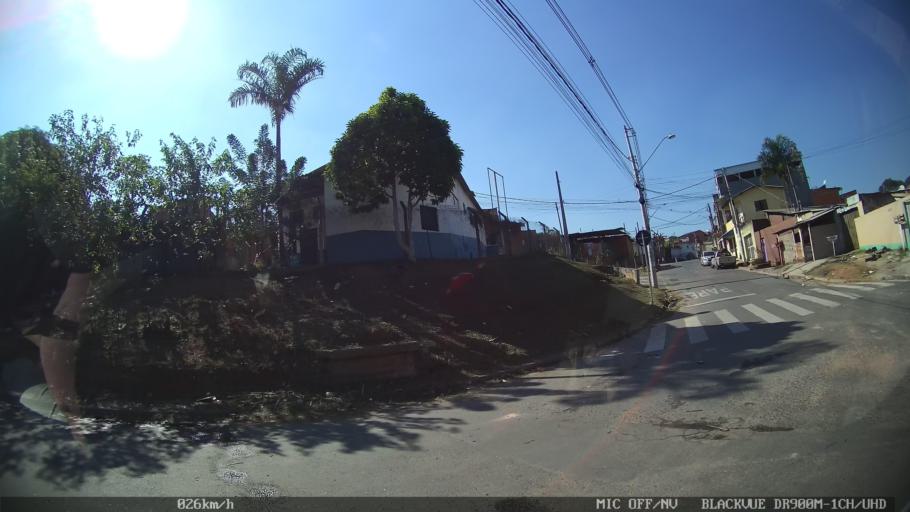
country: BR
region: Sao Paulo
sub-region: Campinas
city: Campinas
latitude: -22.9412
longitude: -47.0851
